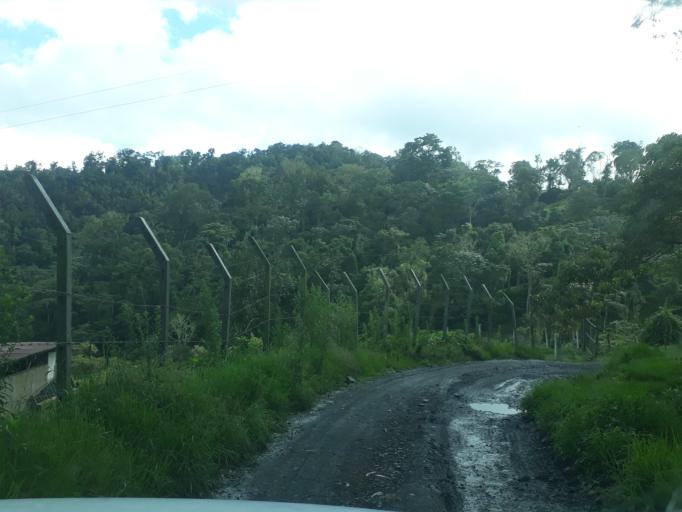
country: CO
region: Cundinamarca
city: Carmen de Carupa
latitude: 5.3425
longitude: -74.0527
